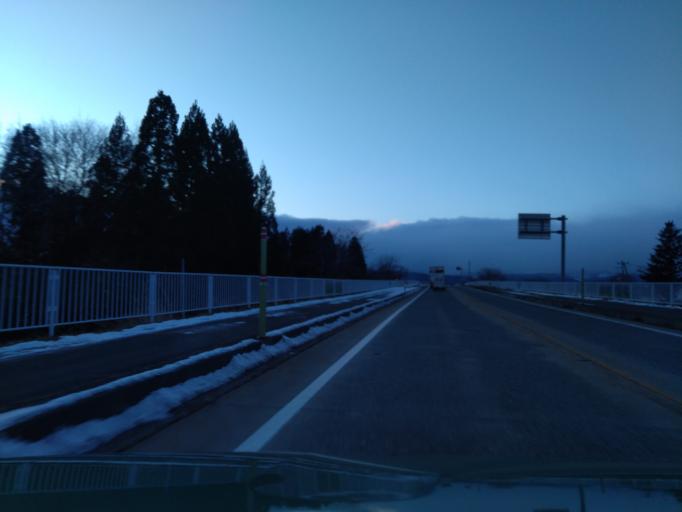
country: JP
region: Iwate
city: Shizukuishi
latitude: 39.6902
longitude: 140.9894
